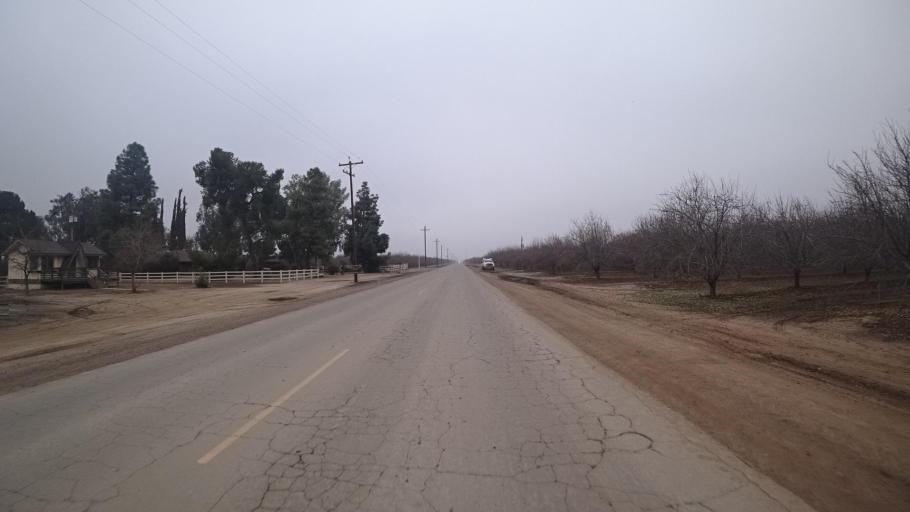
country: US
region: California
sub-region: Kern County
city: Greenfield
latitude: 35.2379
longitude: -119.0424
